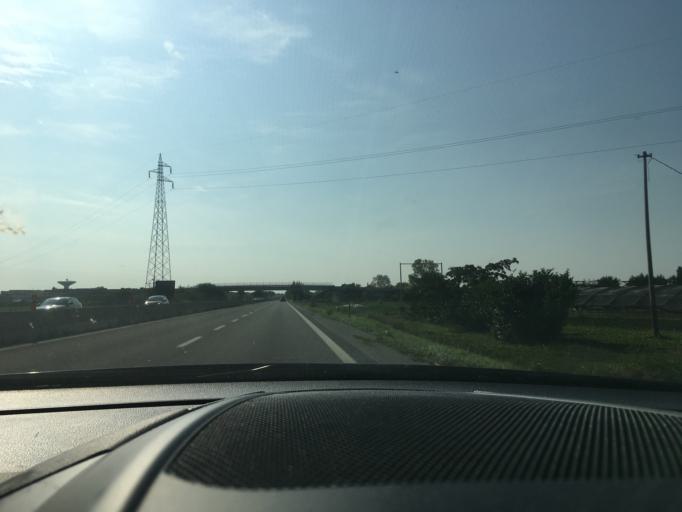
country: IT
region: Emilia-Romagna
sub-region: Provincia di Rimini
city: Bellaria-Igea Marina
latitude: 44.1352
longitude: 12.4629
